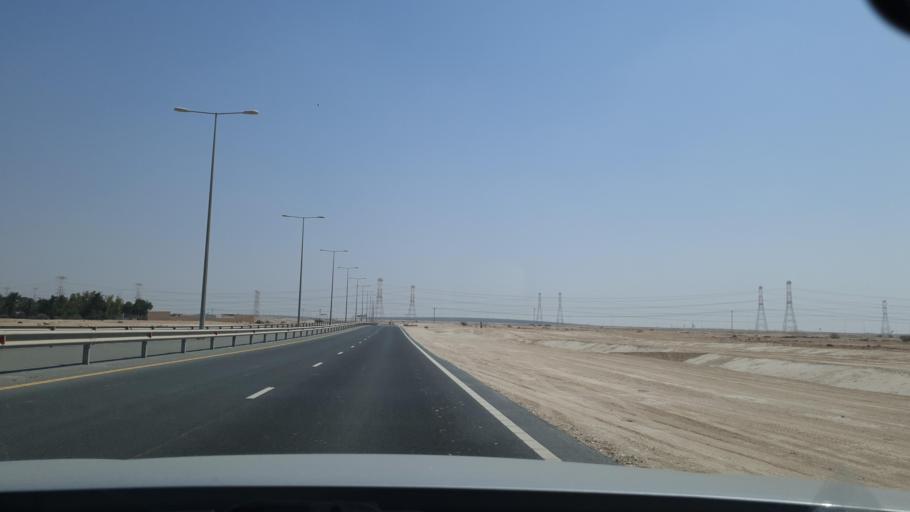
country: QA
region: Baladiyat az Za`ayin
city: Az Za`ayin
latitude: 25.6218
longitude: 51.3466
